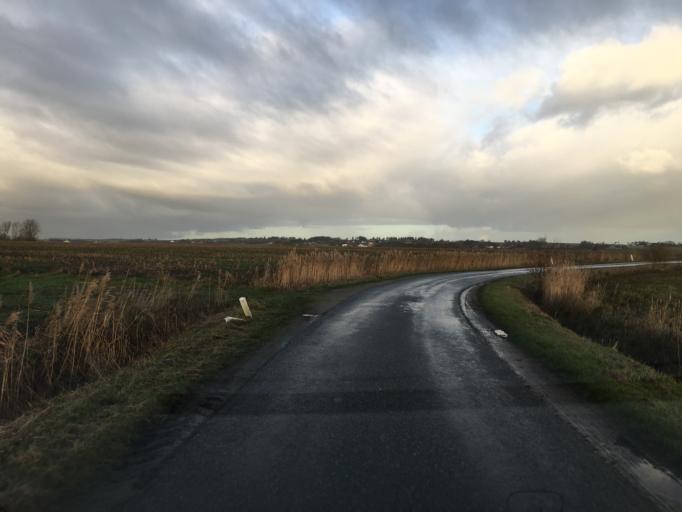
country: DK
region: South Denmark
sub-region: Tonder Kommune
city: Sherrebek
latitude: 55.1431
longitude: 8.8238
